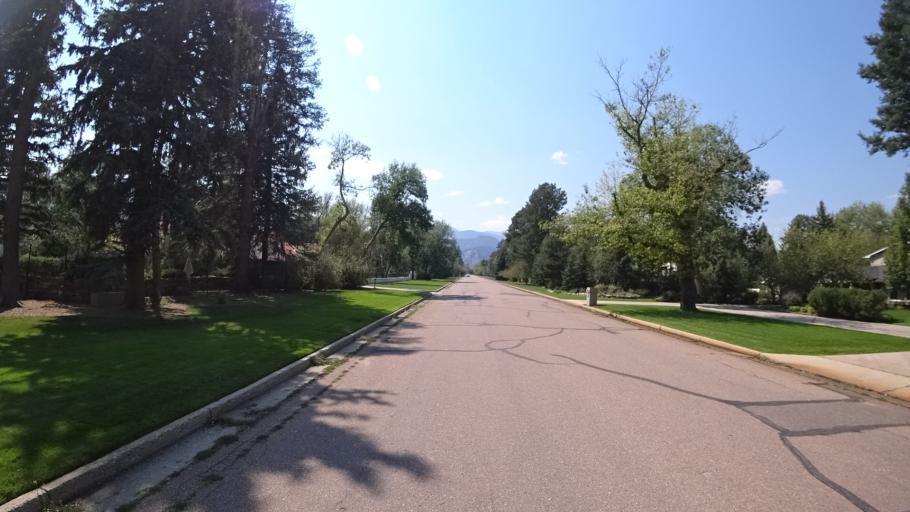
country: US
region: Colorado
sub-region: El Paso County
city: Colorado Springs
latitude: 38.7945
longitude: -104.8403
